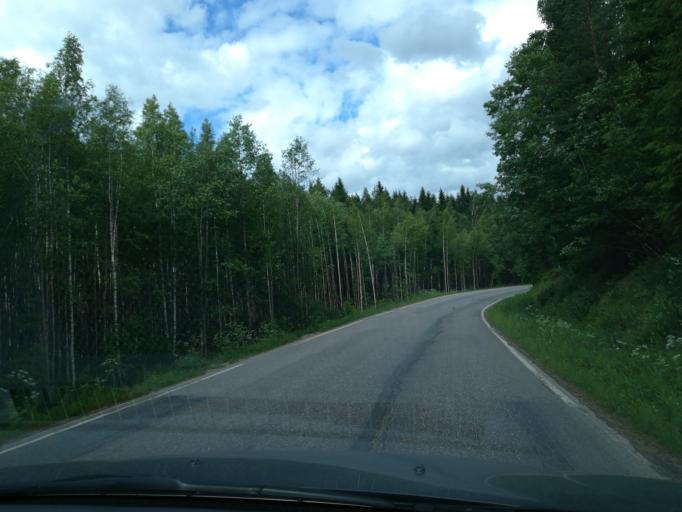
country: FI
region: South Karelia
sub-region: Lappeenranta
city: Savitaipale
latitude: 61.2193
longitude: 27.6947
